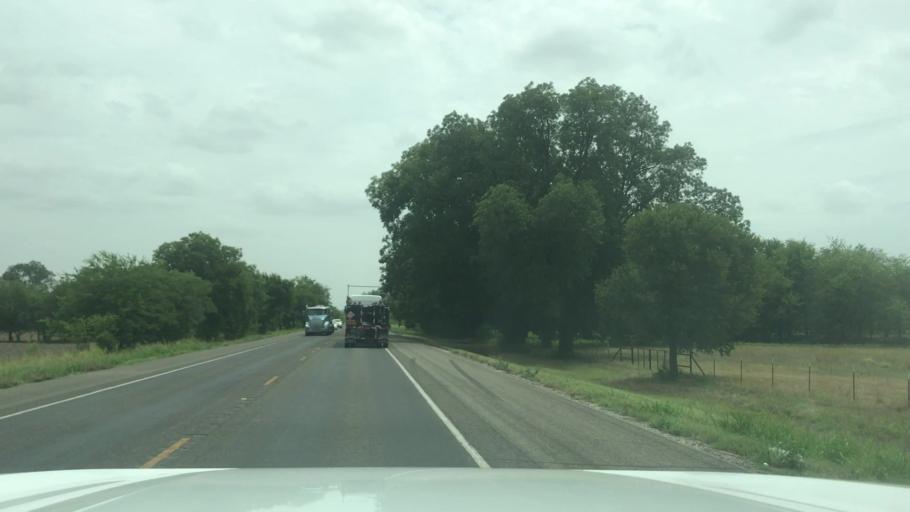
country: US
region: Texas
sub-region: Bosque County
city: Valley Mills
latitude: 31.6712
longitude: -97.5036
